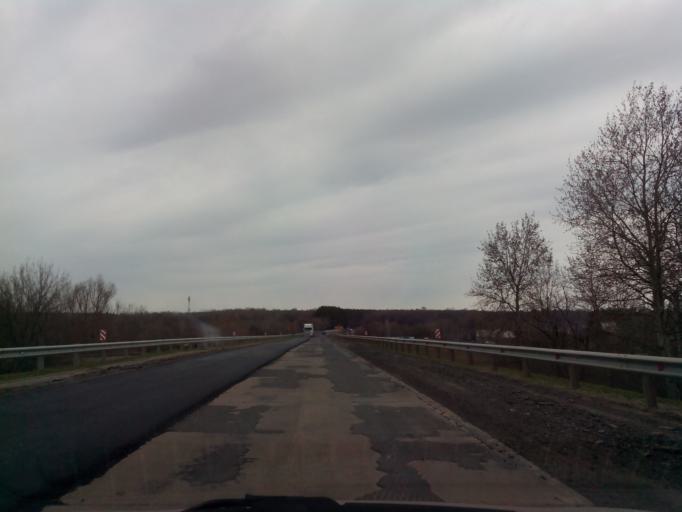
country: RU
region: Tambov
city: Znamenka
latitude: 52.5277
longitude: 41.3590
